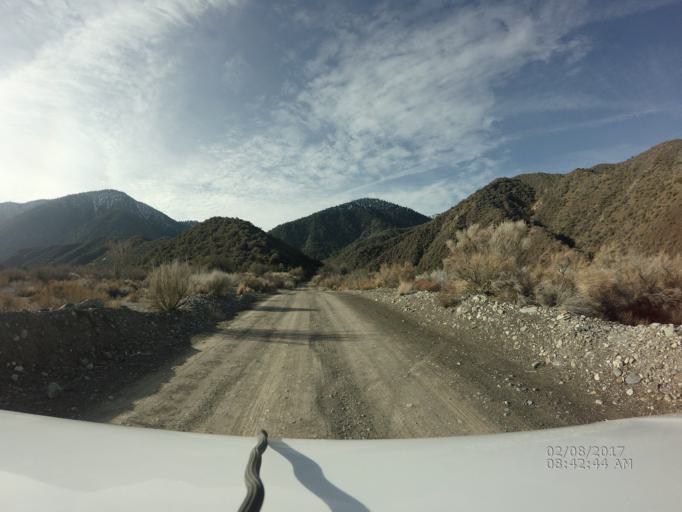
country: US
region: California
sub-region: San Bernardino County
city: Pinon Hills
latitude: 34.4073
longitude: -117.8225
